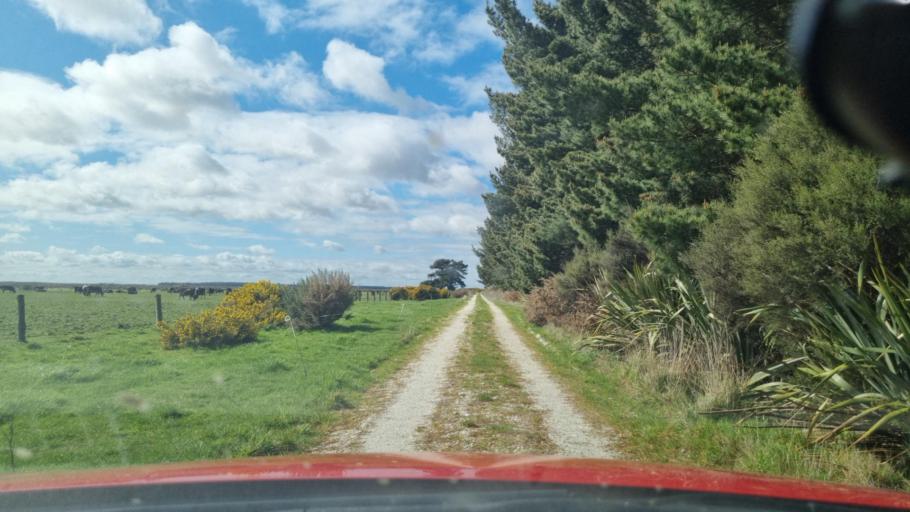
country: NZ
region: Southland
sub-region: Invercargill City
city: Invercargill
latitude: -46.4920
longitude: 168.4406
